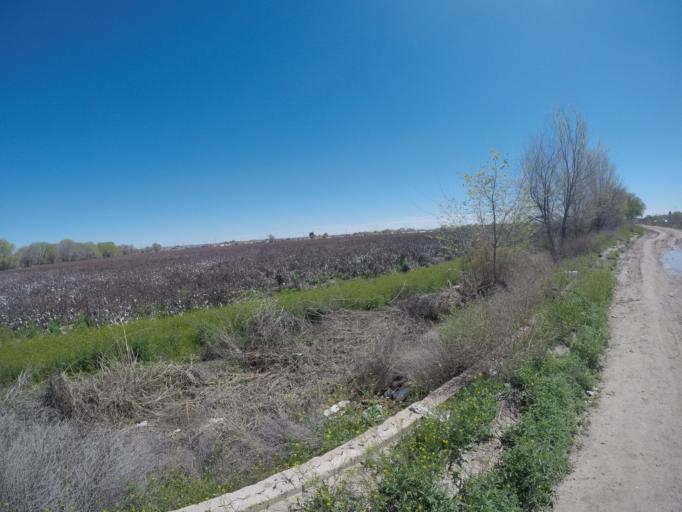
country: US
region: Texas
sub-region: El Paso County
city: Socorro Mission Number 1 Colonia
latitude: 31.6153
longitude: -106.3174
